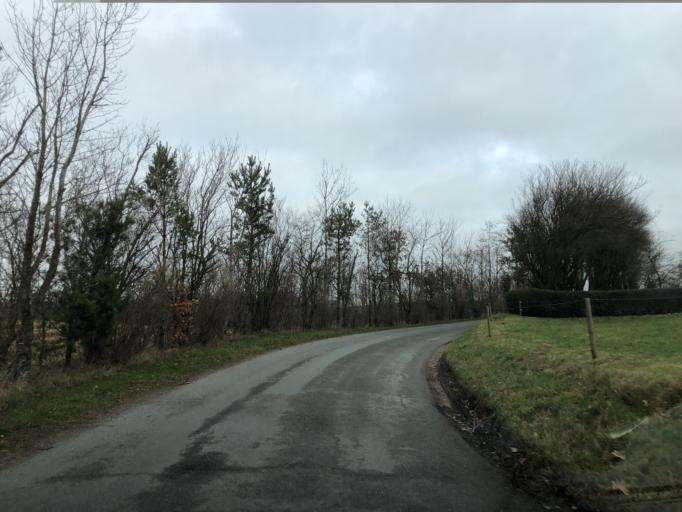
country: DK
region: Central Jutland
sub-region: Viborg Kommune
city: Stoholm
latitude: 56.4498
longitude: 9.1075
